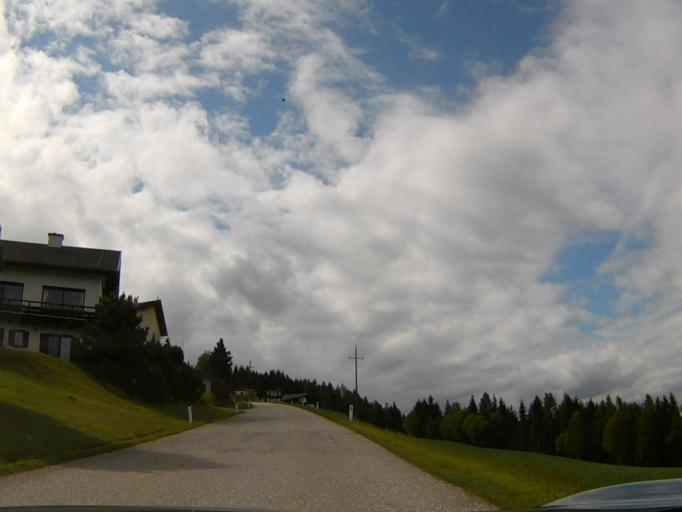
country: AT
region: Carinthia
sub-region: Politischer Bezirk Villach Land
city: Stockenboi
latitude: 46.7370
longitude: 13.5577
